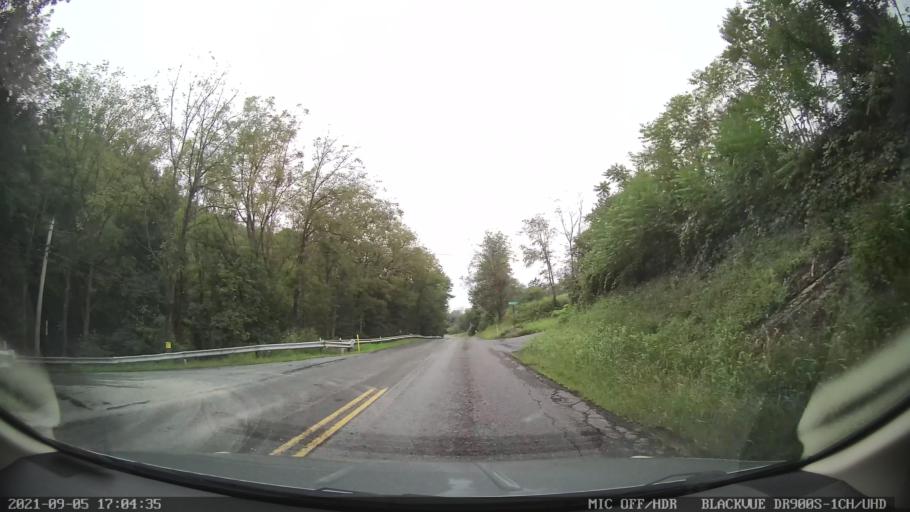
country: US
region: Pennsylvania
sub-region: Lehigh County
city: Breinigsville
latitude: 40.5762
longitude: -75.6828
